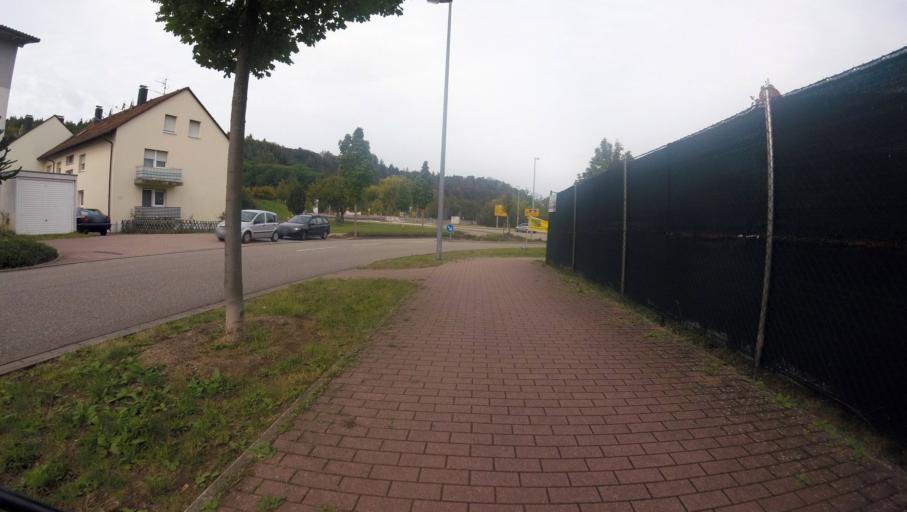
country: DE
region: Baden-Wuerttemberg
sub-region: Karlsruhe Region
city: Gaggenau
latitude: 48.8076
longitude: 8.3054
